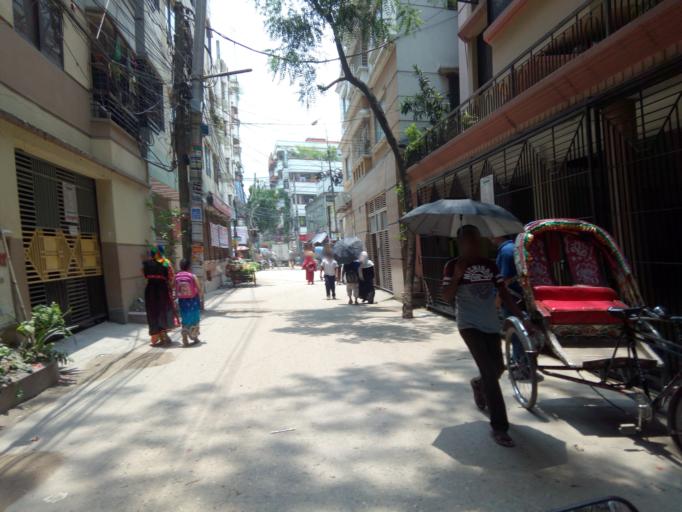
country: BD
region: Dhaka
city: Paltan
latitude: 23.7624
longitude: 90.4303
